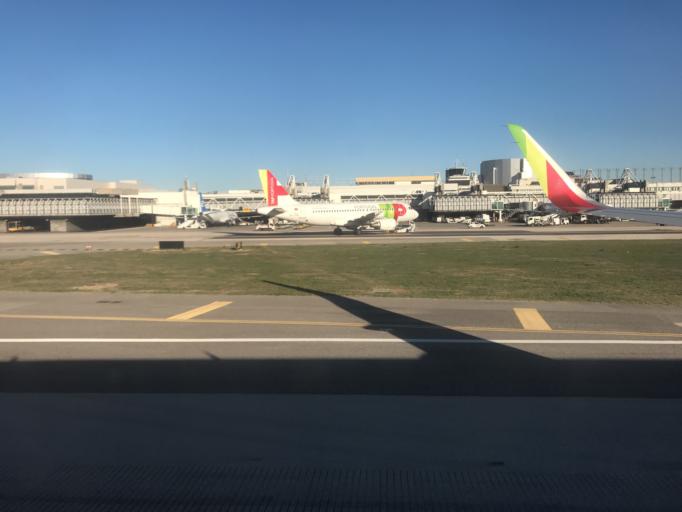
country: PT
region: Lisbon
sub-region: Loures
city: Moscavide
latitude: 38.7696
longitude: -9.1326
